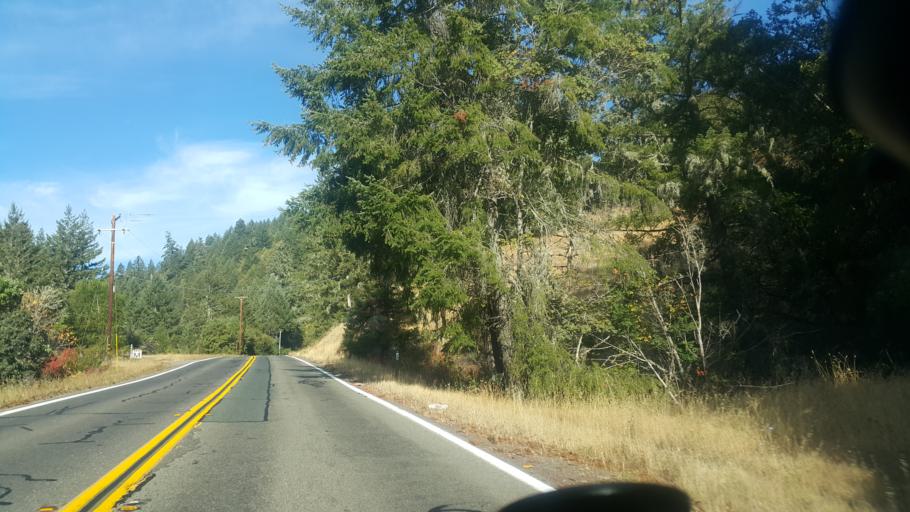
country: US
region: California
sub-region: Mendocino County
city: Brooktrails
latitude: 39.3877
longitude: -123.4284
